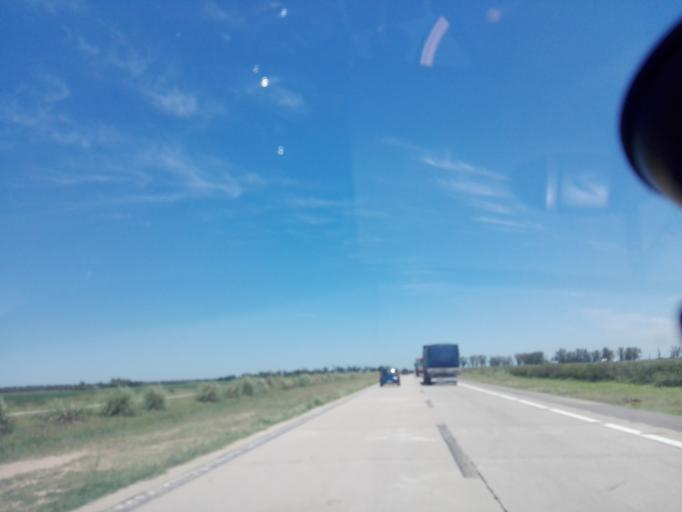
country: AR
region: Cordoba
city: General Roca
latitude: -32.6936
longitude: -61.9638
